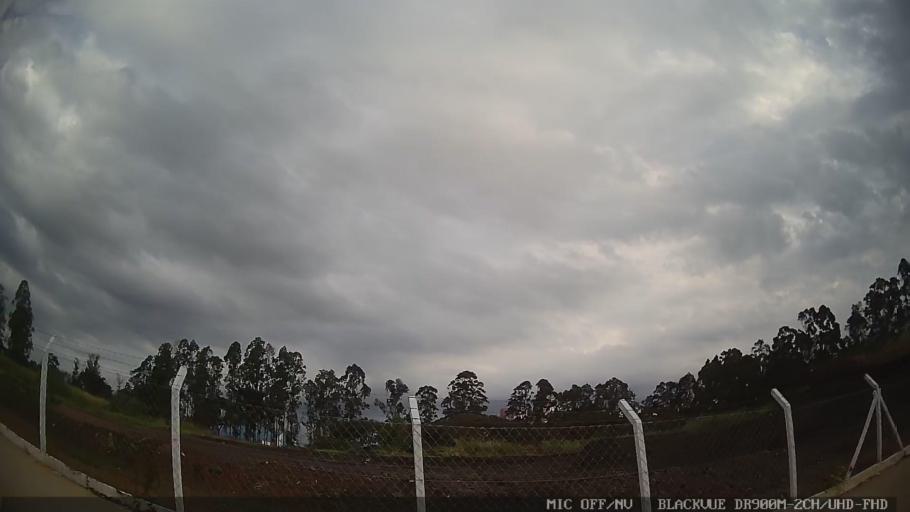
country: BR
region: Sao Paulo
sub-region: Indaiatuba
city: Indaiatuba
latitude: -23.1091
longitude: -47.2232
